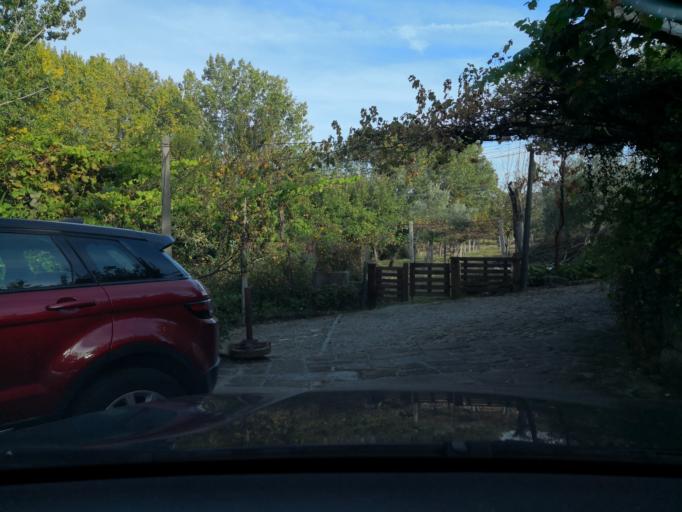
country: PT
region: Vila Real
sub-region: Vila Real
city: Vila Real
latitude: 41.3132
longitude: -7.7394
